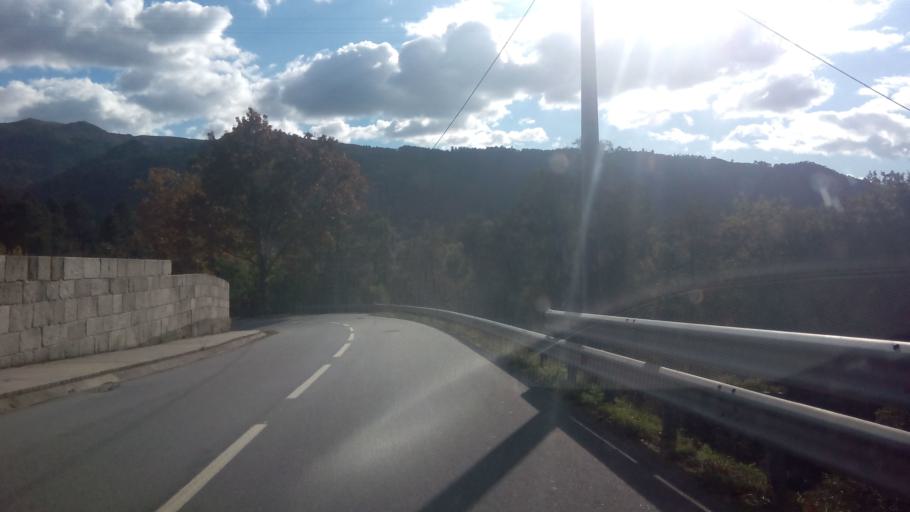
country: PT
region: Porto
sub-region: Amarante
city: Amarante
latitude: 41.2548
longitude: -8.0335
